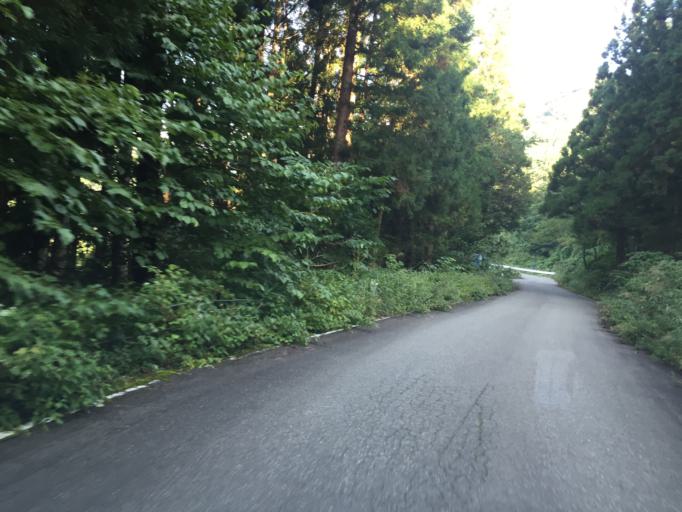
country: JP
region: Fukushima
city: Inawashiro
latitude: 37.4326
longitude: 139.9768
